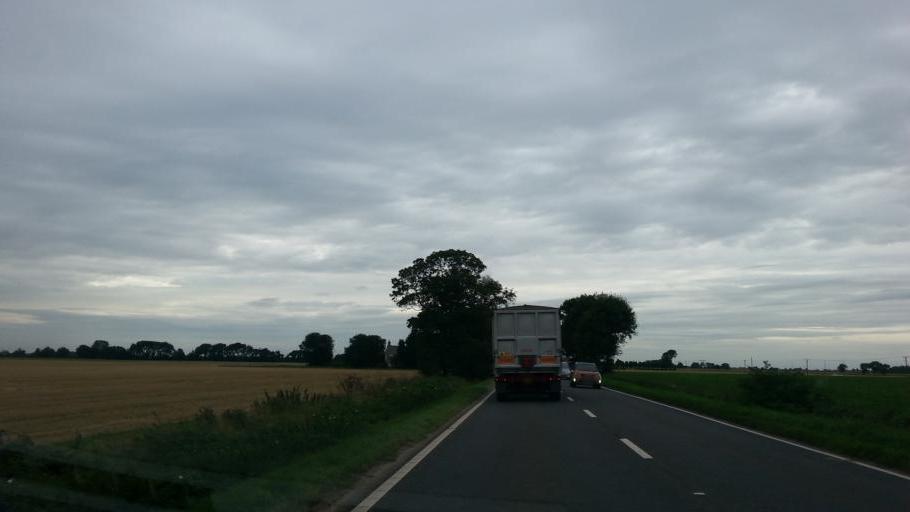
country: GB
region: England
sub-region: Peterborough
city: Thorney
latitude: 52.6163
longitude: -0.1485
